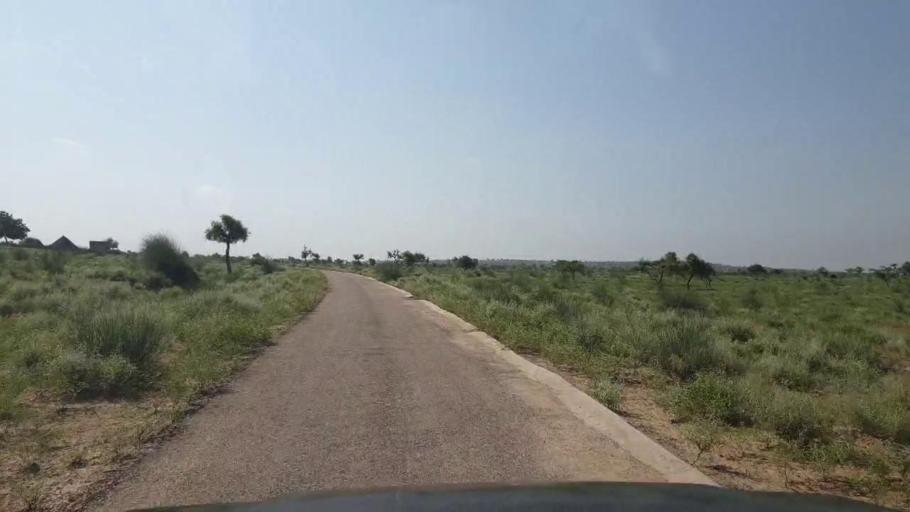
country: PK
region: Sindh
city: Islamkot
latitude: 25.1815
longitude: 70.3927
